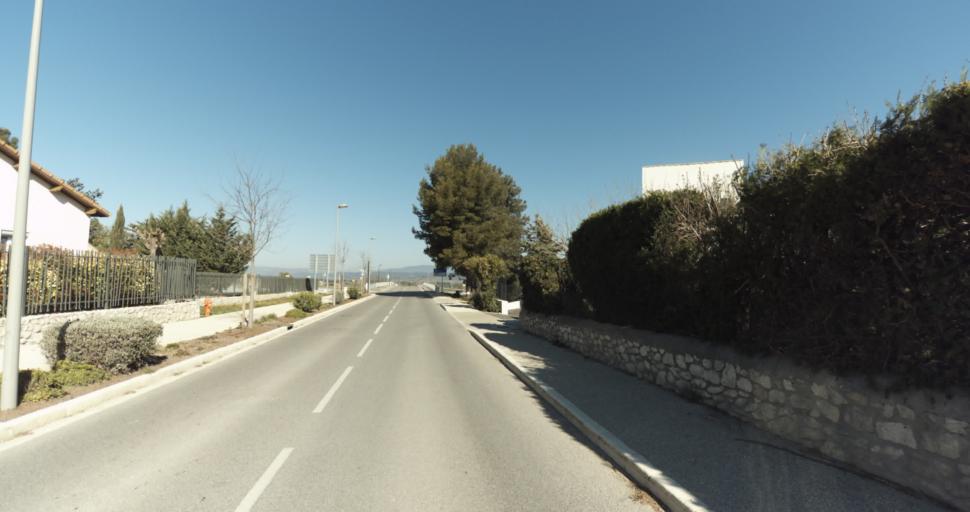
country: FR
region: Provence-Alpes-Cote d'Azur
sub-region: Departement des Bouches-du-Rhone
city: Meyrargues
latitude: 43.6416
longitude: 5.5247
